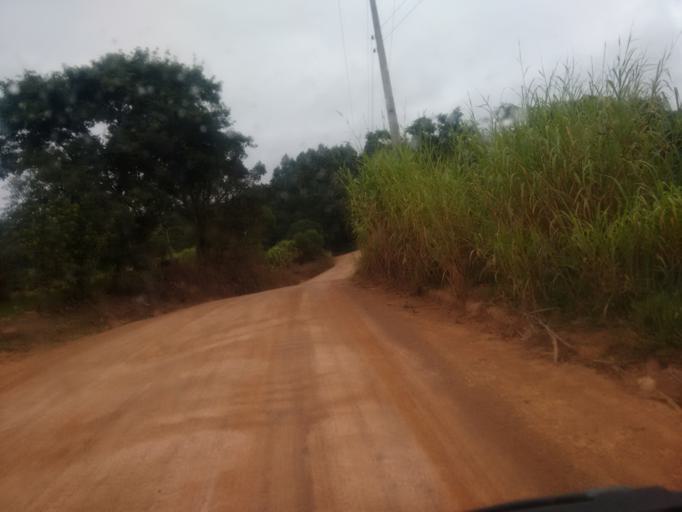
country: BR
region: Rio Grande do Sul
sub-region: Camaqua
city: Camaqua
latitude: -30.7330
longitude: -51.8394
